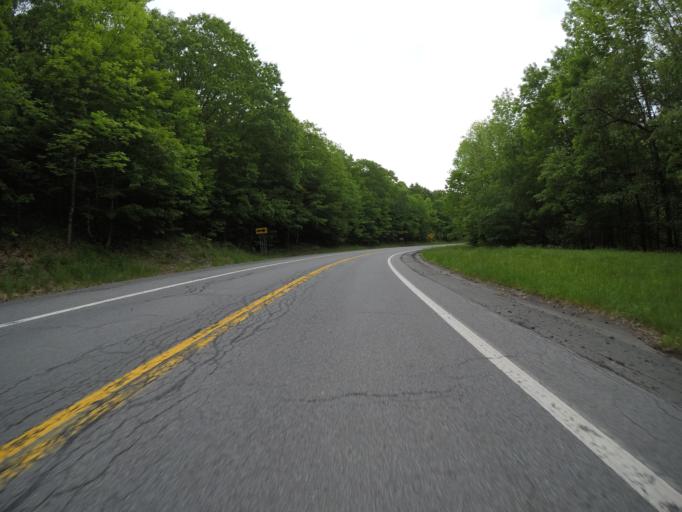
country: US
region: New York
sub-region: Sullivan County
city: Livingston Manor
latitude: 42.0693
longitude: -74.8789
